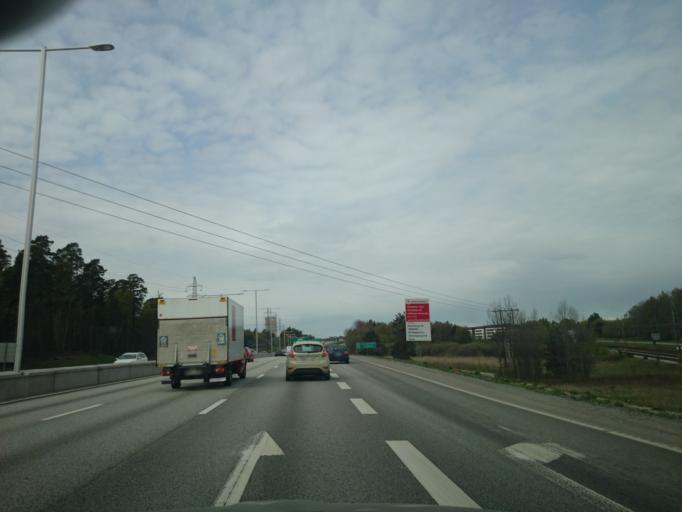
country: SE
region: Stockholm
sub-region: Solna Kommun
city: Rasunda
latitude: 59.3948
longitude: 17.9856
